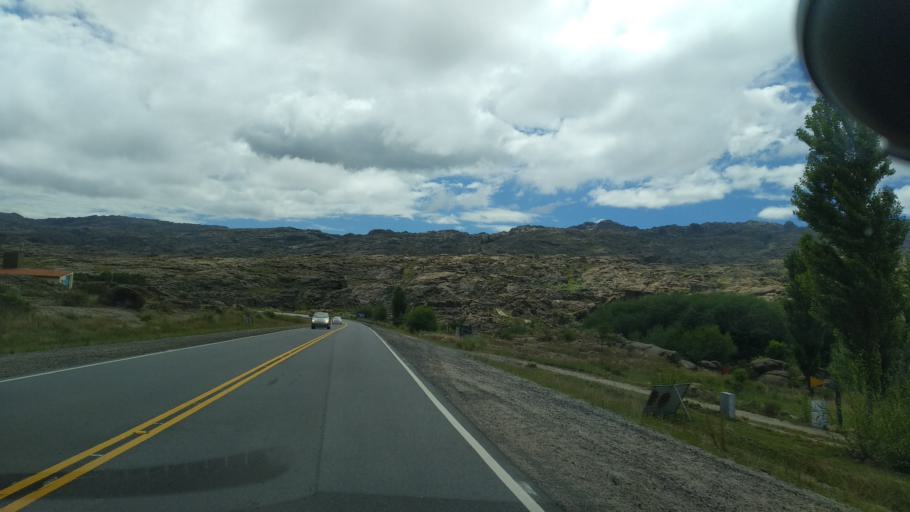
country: AR
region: Cordoba
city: Mina Clavero
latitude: -31.7347
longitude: -64.9038
